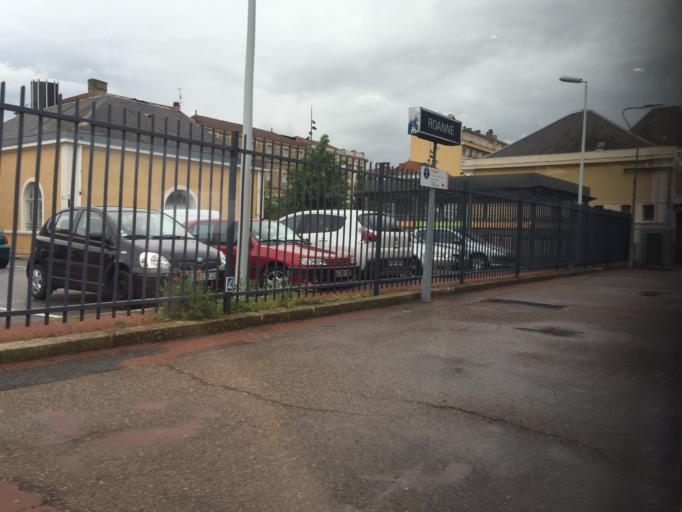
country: FR
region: Rhone-Alpes
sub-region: Departement de la Loire
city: Roanne
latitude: 46.0401
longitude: 4.0628
